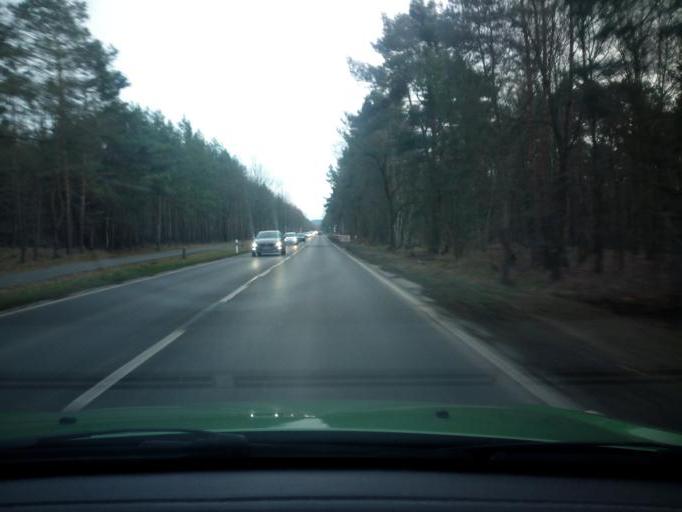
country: DE
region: Berlin
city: Berlin Koepenick
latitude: 52.4360
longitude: 13.5994
